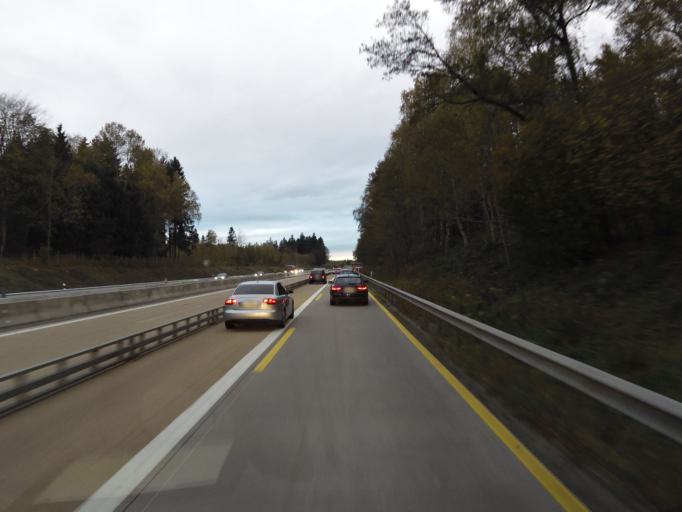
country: DE
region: Bavaria
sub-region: Upper Bavaria
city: Raubling
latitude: 47.7657
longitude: 12.1020
